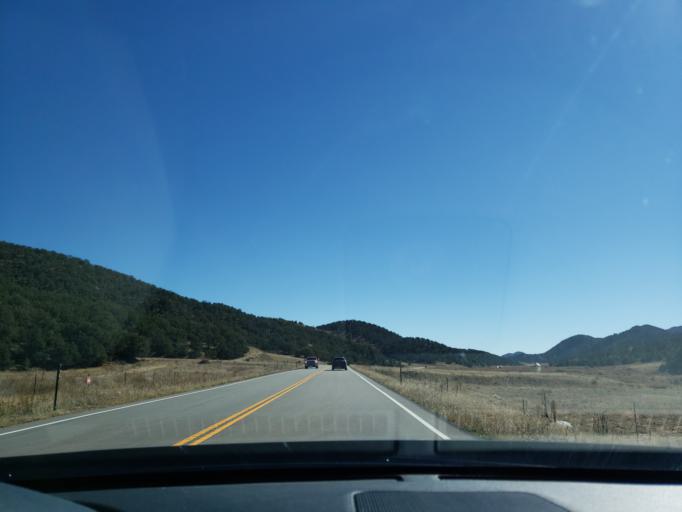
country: US
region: Colorado
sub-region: Fremont County
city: Canon City
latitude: 38.6380
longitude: -105.4689
